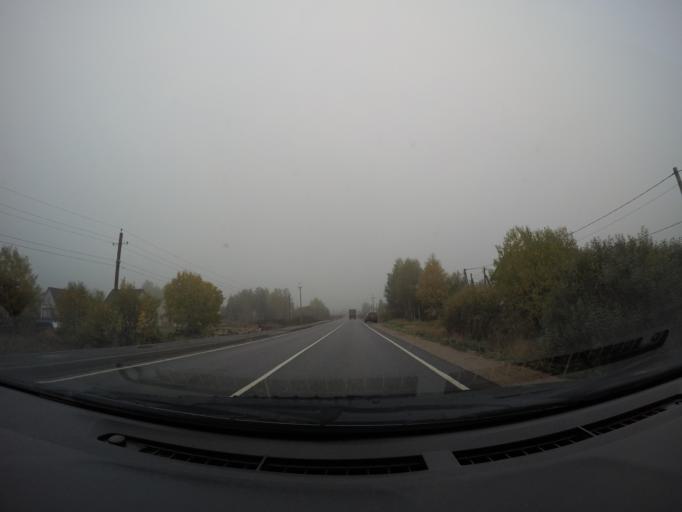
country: RU
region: Moskovskaya
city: Rumyantsevo
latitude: 55.8466
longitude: 36.4925
